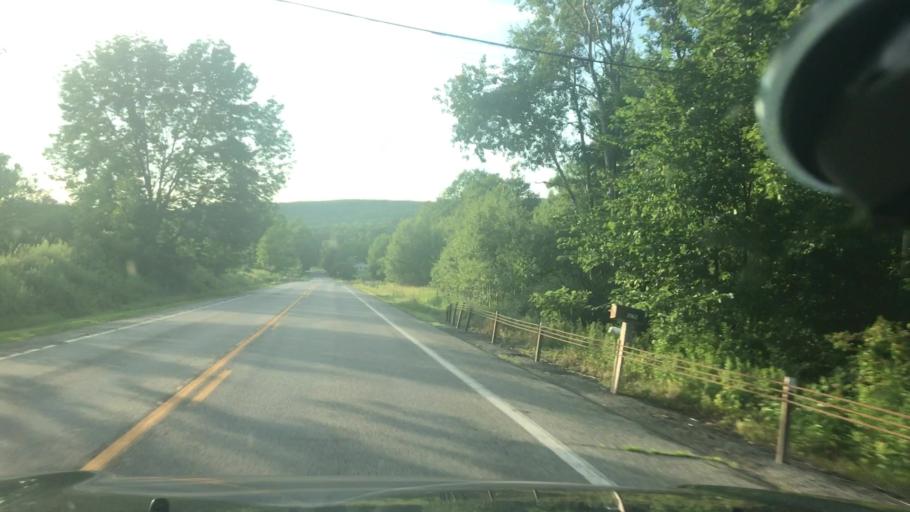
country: US
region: New York
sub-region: Otsego County
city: Unadilla
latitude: 42.3304
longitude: -75.2336
